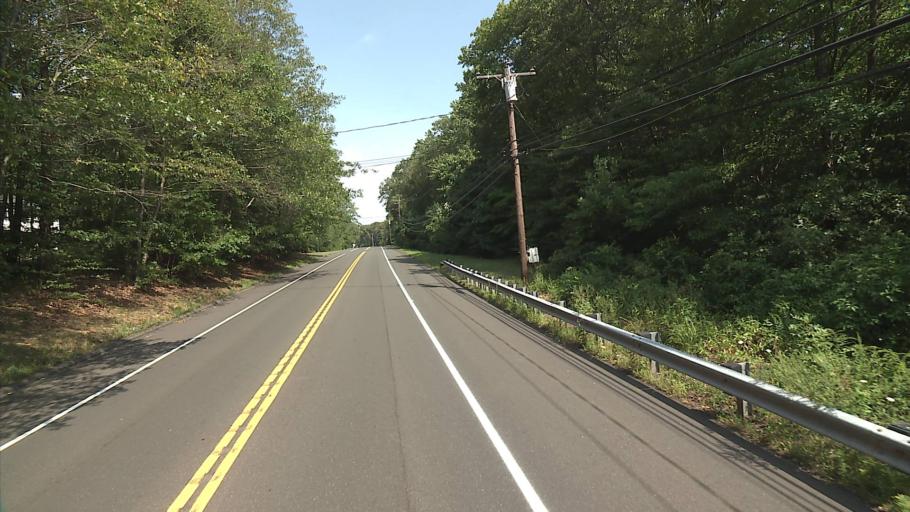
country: US
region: Connecticut
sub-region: New Haven County
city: Guilford
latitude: 41.3643
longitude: -72.6379
